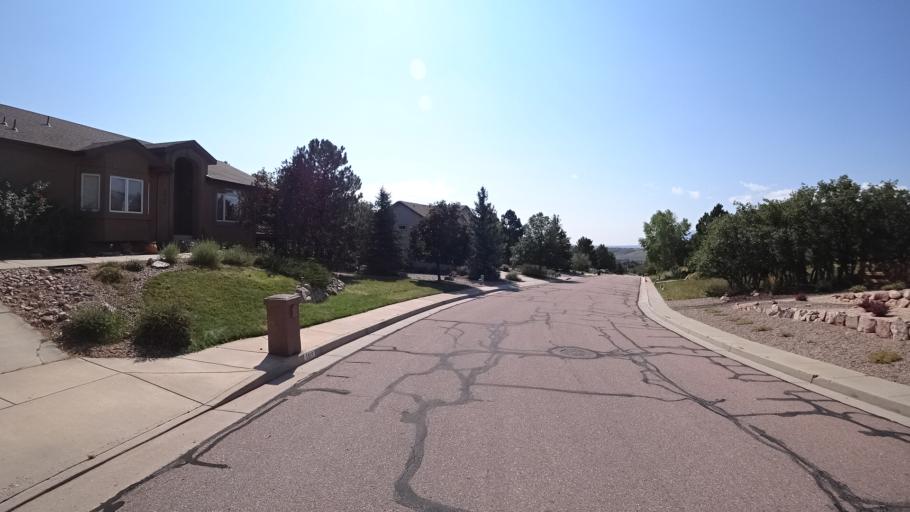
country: US
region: Colorado
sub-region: El Paso County
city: Manitou Springs
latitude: 38.9111
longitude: -104.8707
